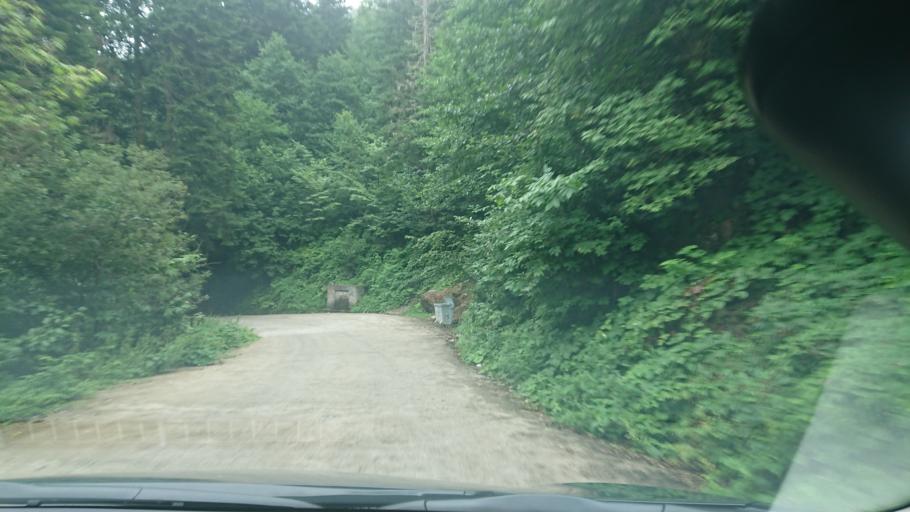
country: TR
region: Gumushane
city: Kurtun
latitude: 40.6654
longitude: 39.0390
